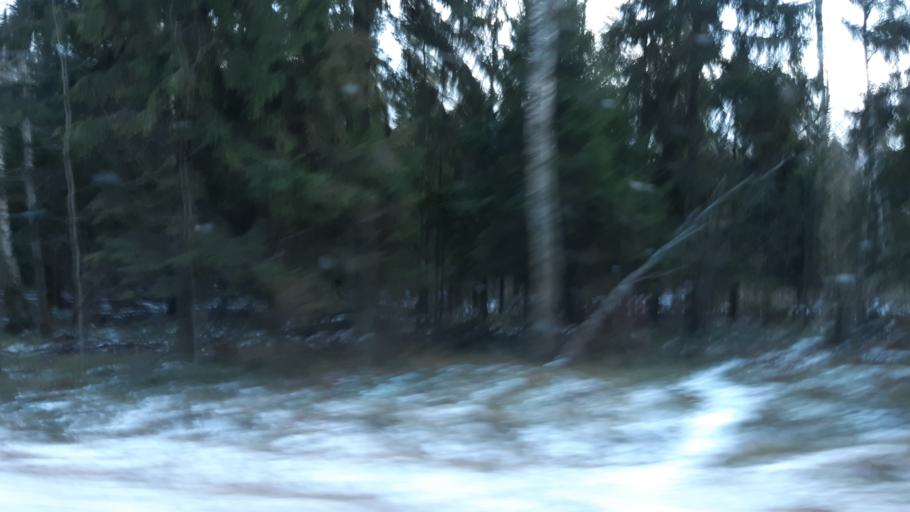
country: RU
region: Moskovskaya
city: Noginsk-9
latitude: 55.9754
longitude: 38.5405
